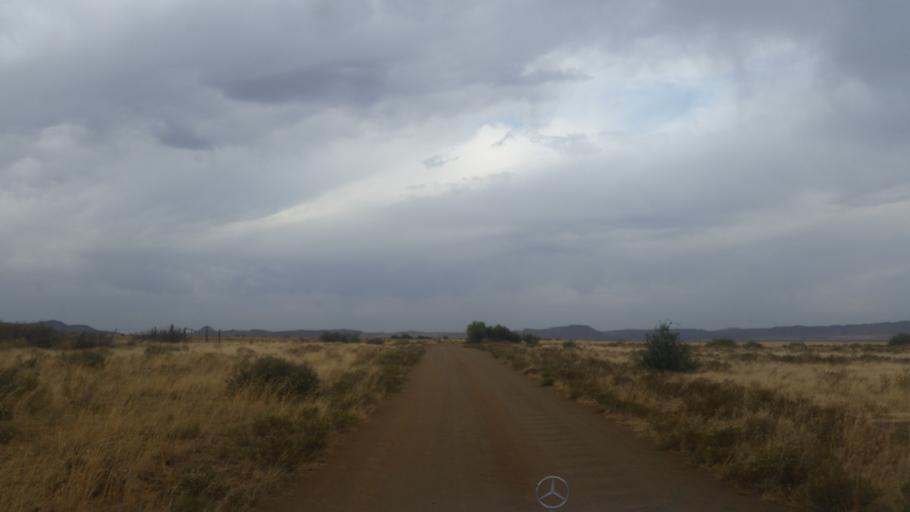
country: ZA
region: Orange Free State
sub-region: Xhariep District Municipality
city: Trompsburg
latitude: -30.5068
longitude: 25.9344
